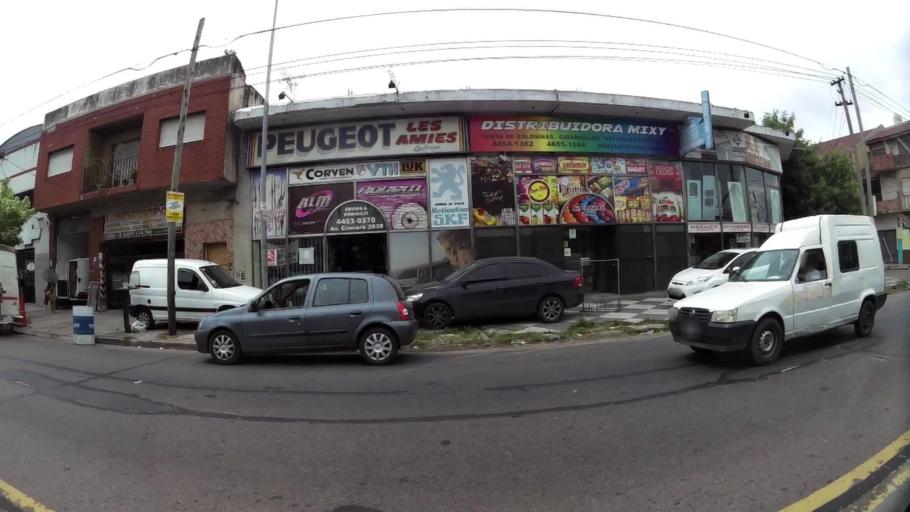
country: AR
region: Buenos Aires
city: San Justo
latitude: -34.6855
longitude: -58.5192
